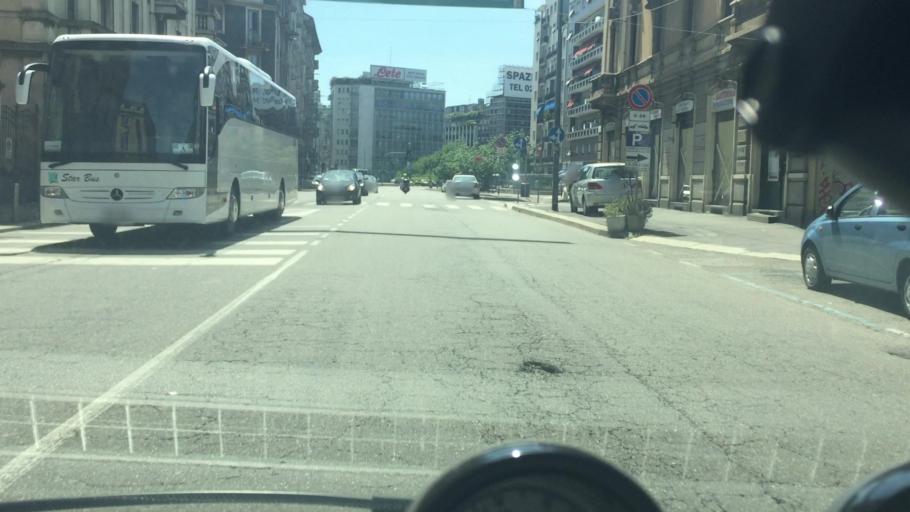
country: IT
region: Lombardy
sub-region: Citta metropolitana di Milano
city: Milano
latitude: 45.4870
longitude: 9.2198
